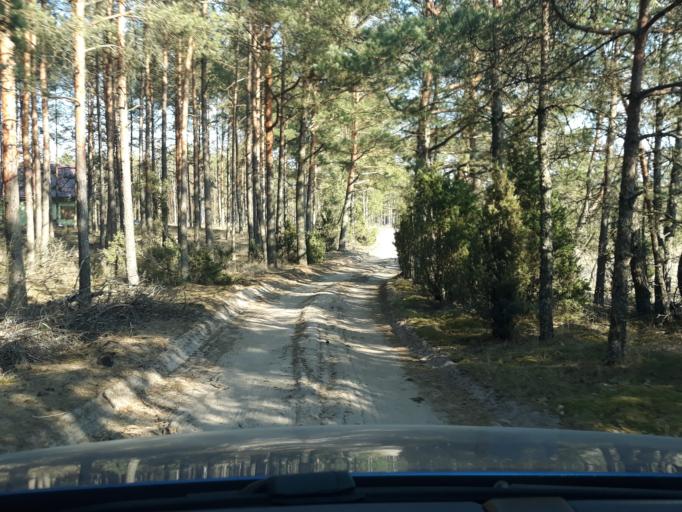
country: PL
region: Pomeranian Voivodeship
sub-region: Powiat bytowski
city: Lipnica
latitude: 53.9191
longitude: 17.4566
